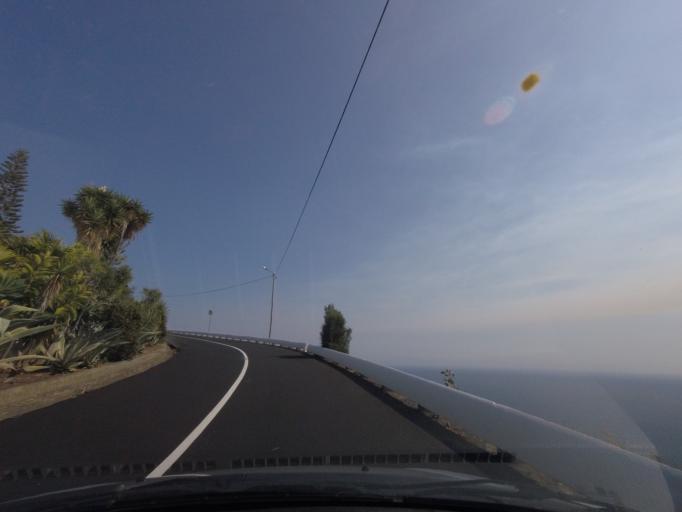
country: PT
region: Madeira
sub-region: Ribeira Brava
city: Campanario
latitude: 32.6665
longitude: -17.0505
